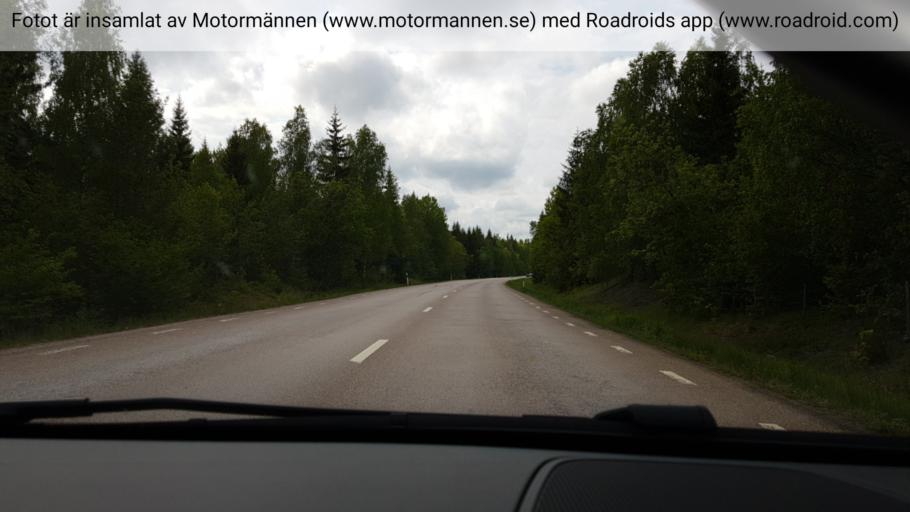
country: SE
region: Uppsala
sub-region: Osthammars Kommun
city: Osterbybruk
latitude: 60.1954
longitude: 17.8238
